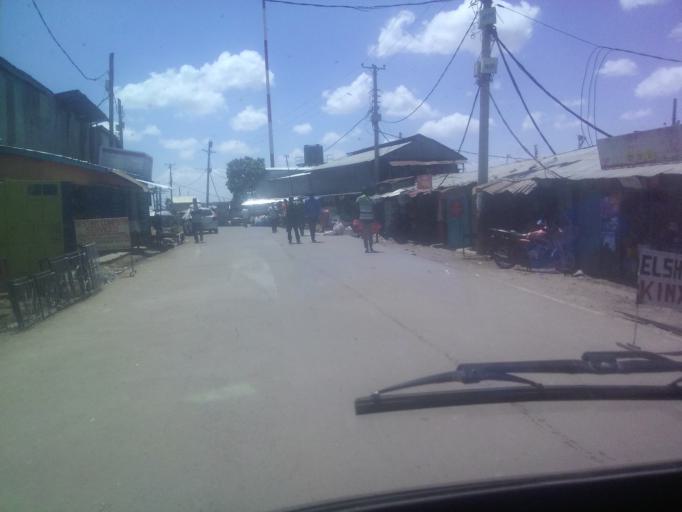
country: KE
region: Nairobi Area
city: Nairobi
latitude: -1.3125
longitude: 36.7943
